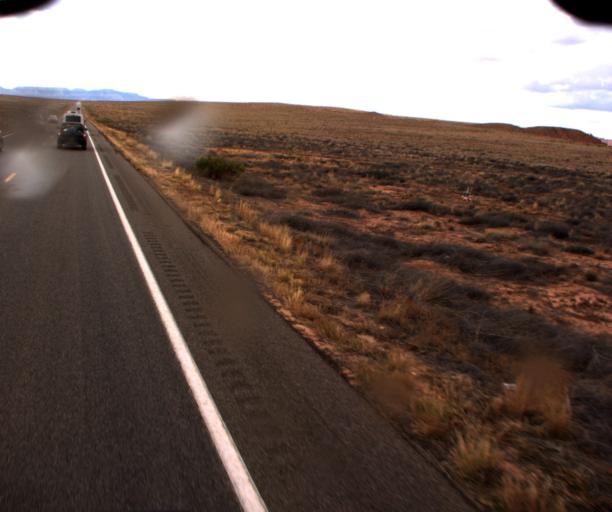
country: US
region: Arizona
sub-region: Navajo County
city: Kayenta
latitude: 36.7529
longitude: -110.0581
